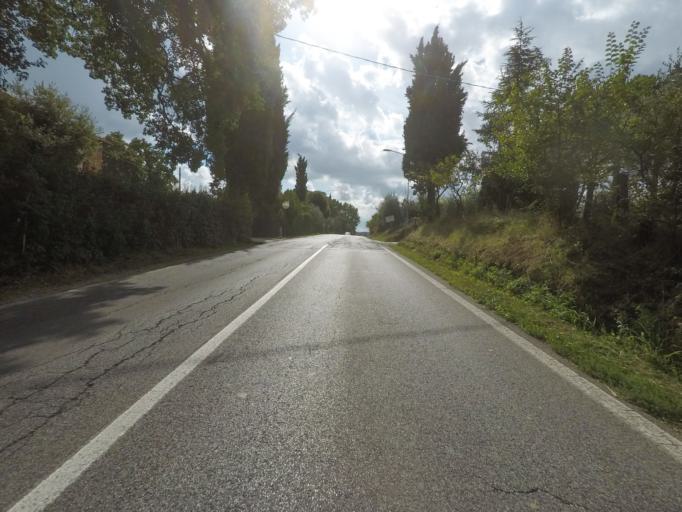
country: IT
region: Tuscany
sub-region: Provincia di Siena
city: Torrita di Siena
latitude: 43.1755
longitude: 11.7732
